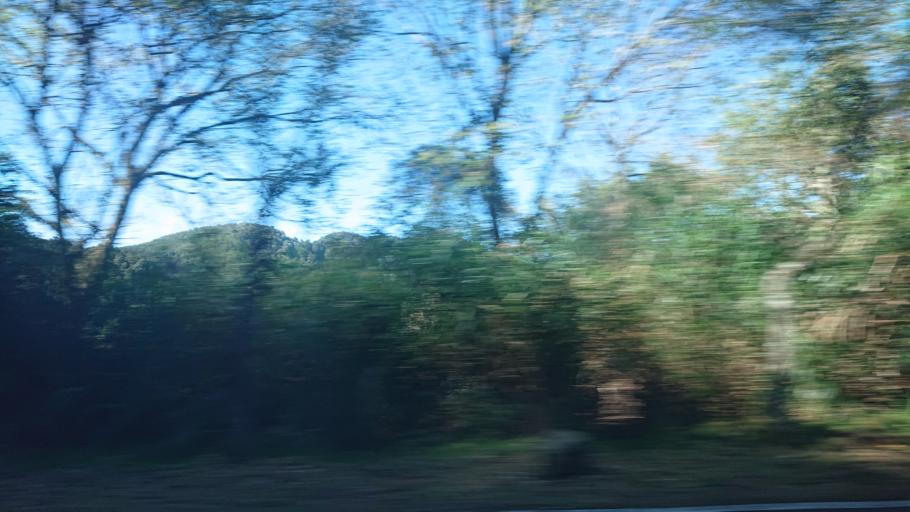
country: TW
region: Taiwan
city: Lugu
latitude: 23.4759
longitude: 120.8511
